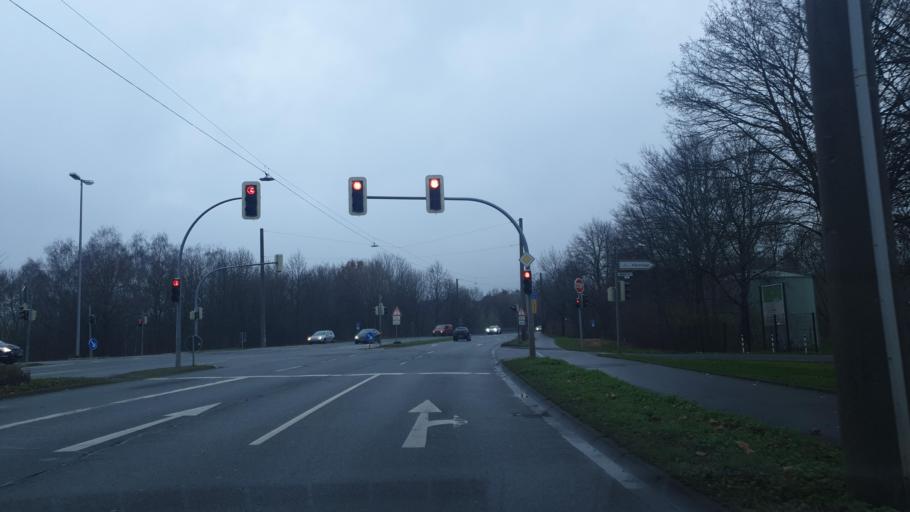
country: DE
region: North Rhine-Westphalia
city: Bad Oeynhausen
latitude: 52.2166
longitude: 8.8190
